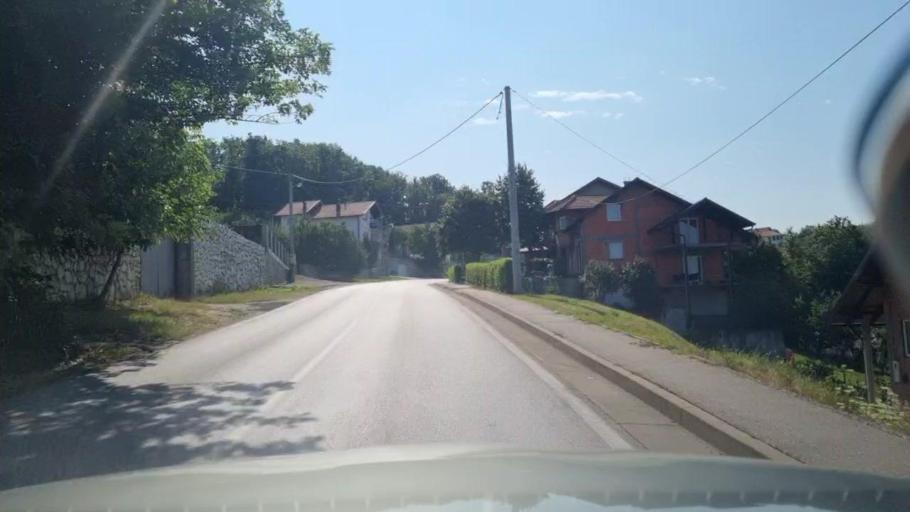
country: BA
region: Federation of Bosnia and Herzegovina
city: Gradacac
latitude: 44.8761
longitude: 18.4397
